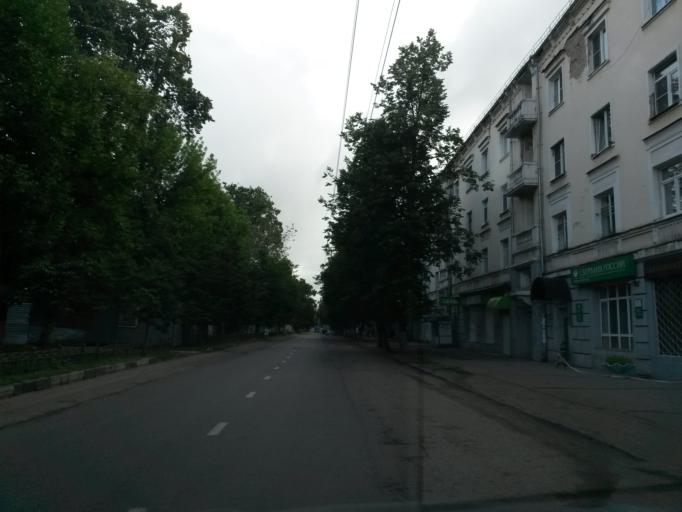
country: RU
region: Jaroslavl
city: Yaroslavl
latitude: 57.6406
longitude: 39.8770
